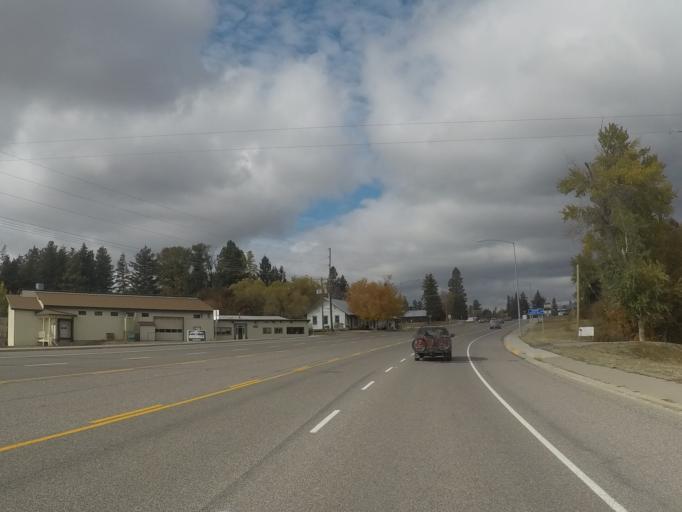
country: US
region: Montana
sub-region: Flathead County
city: Columbia Falls
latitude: 48.3678
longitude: -114.1778
